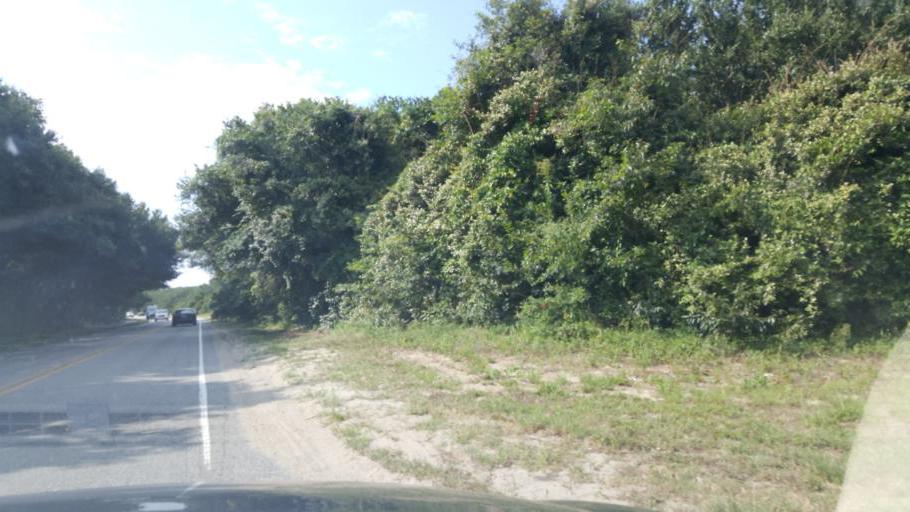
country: US
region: North Carolina
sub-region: Dare County
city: Southern Shores
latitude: 36.1477
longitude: -75.7414
